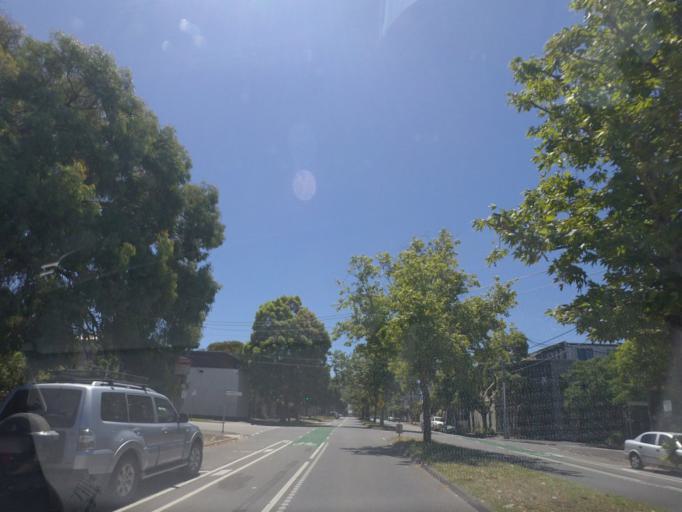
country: AU
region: Victoria
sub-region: Port Phillip
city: South Melbourne
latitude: -37.8370
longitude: 144.9653
